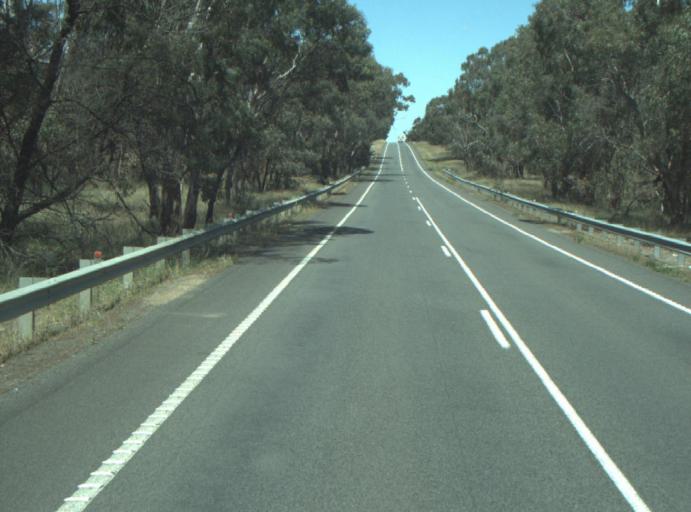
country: AU
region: Victoria
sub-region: Greater Geelong
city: Lara
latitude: -37.9156
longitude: 144.3666
